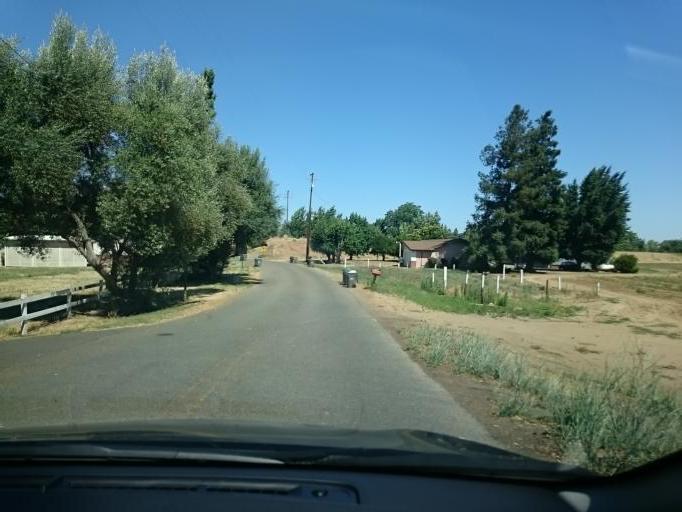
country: US
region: California
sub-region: Yolo County
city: West Sacramento
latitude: 38.5157
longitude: -121.5518
